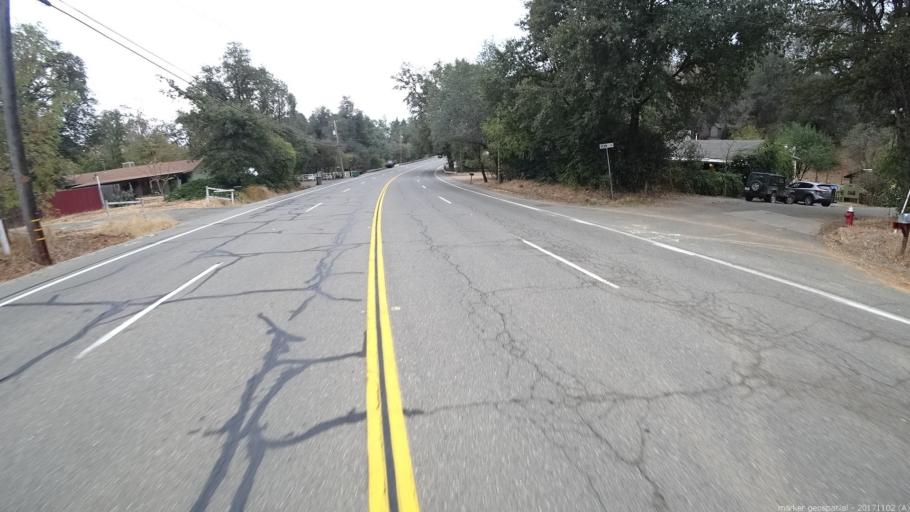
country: US
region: California
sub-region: Shasta County
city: Central Valley (historical)
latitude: 40.6446
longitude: -122.3973
